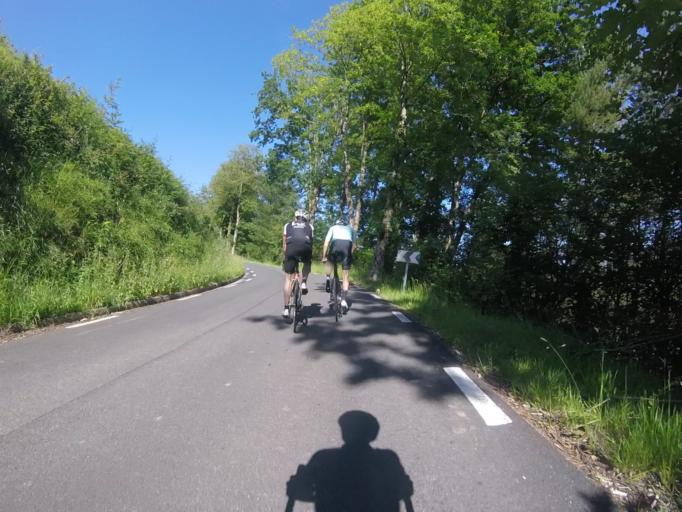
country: ES
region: Basque Country
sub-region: Provincia de Guipuzcoa
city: Beizama
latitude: 43.1393
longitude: -2.2214
